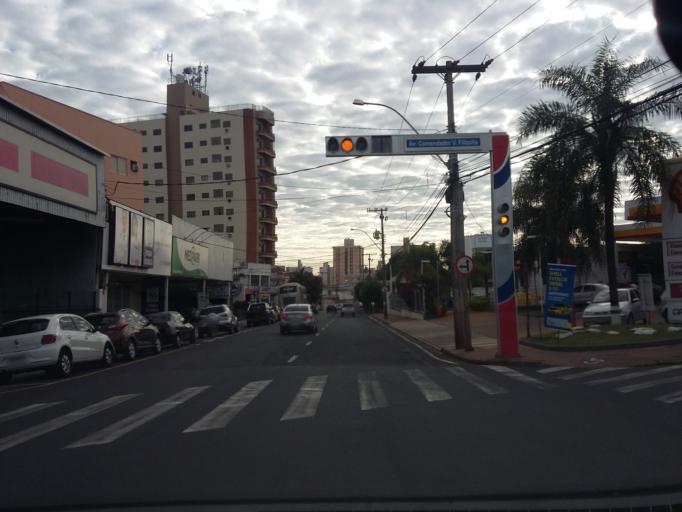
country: BR
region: Sao Paulo
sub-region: Sao Jose Do Rio Preto
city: Sao Jose do Rio Preto
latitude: -20.8230
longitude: -49.3927
